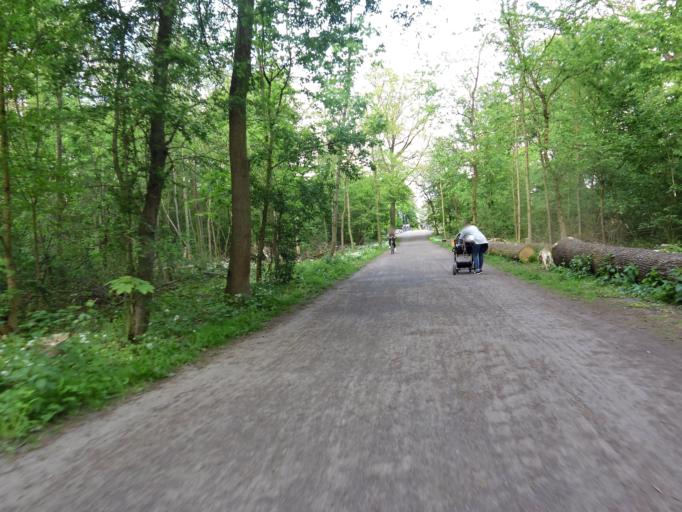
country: DE
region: Saxony
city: Leipzig
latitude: 51.3259
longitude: 12.3544
